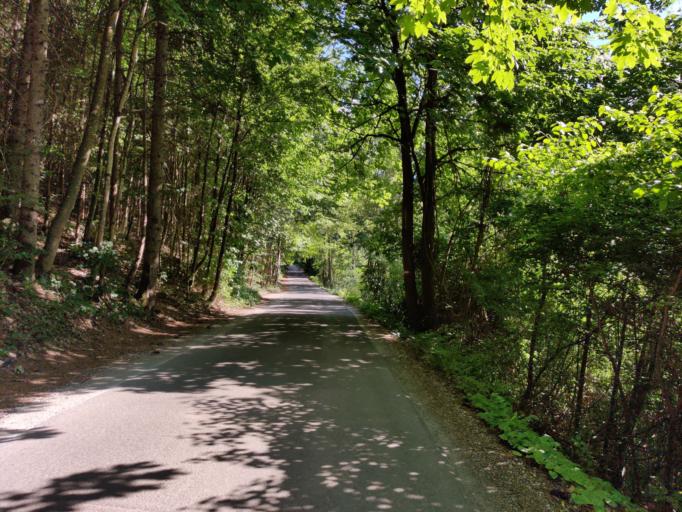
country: AT
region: Styria
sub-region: Graz Stadt
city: Wetzelsdorf
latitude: 47.0390
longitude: 15.3677
